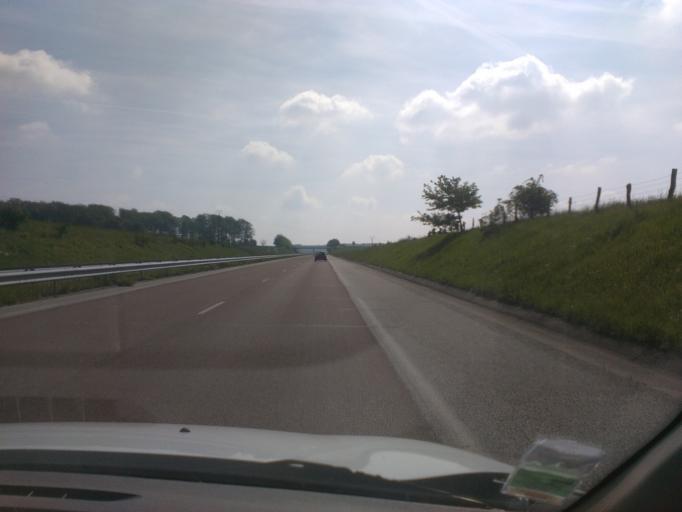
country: FR
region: Lorraine
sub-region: Departement des Vosges
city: Uxegney
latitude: 48.2038
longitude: 6.3606
